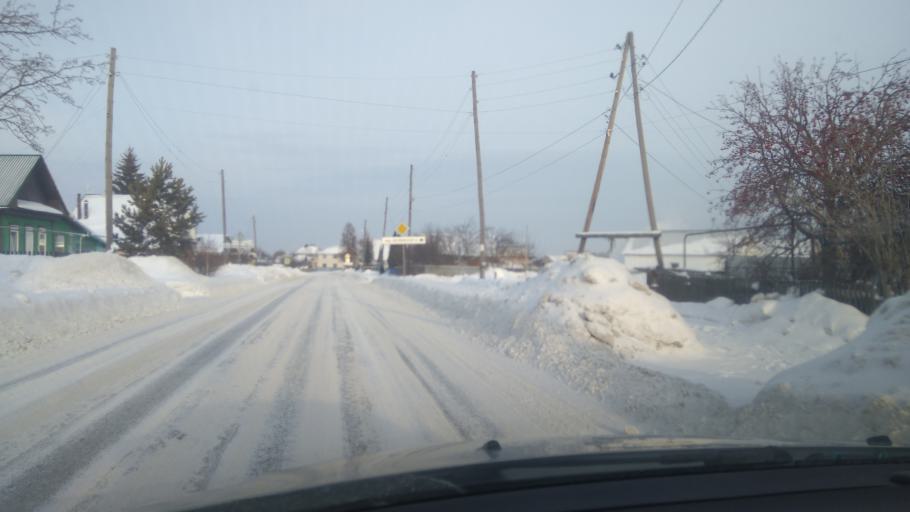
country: RU
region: Sverdlovsk
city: Sukhoy Log
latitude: 56.9054
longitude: 62.0232
